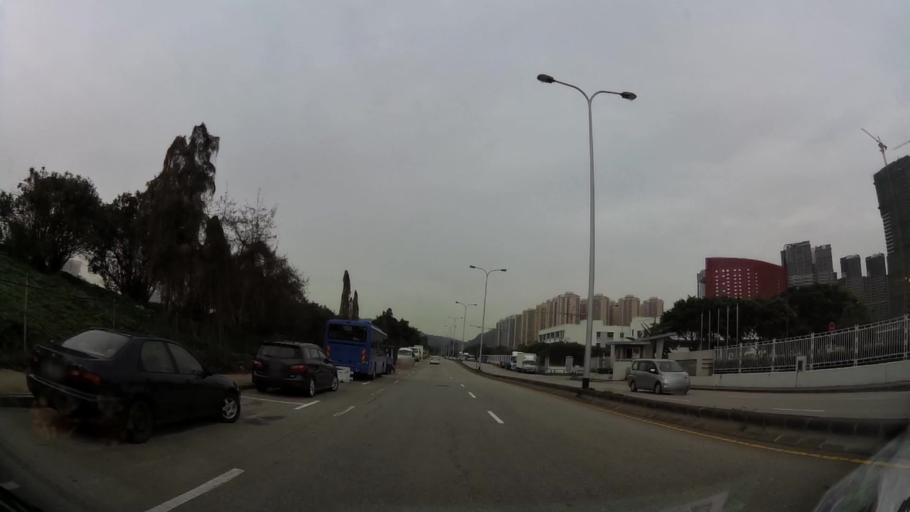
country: MO
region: Macau
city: Macau
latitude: 22.1319
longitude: 113.5551
